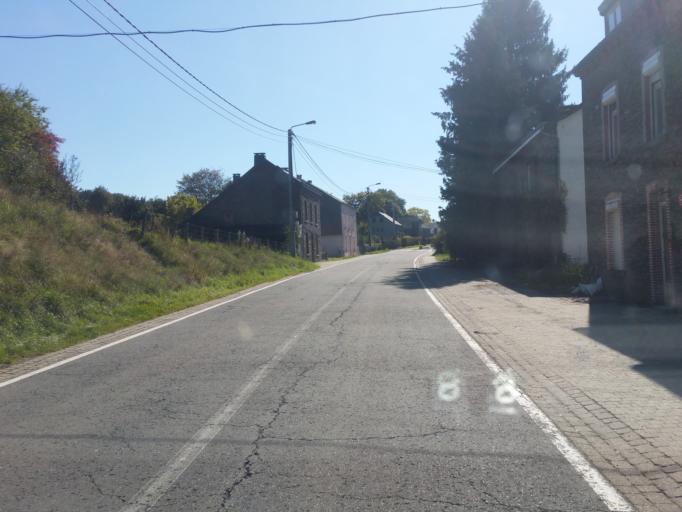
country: BE
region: Wallonia
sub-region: Province du Luxembourg
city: Herbeumont
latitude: 49.7855
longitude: 5.2365
